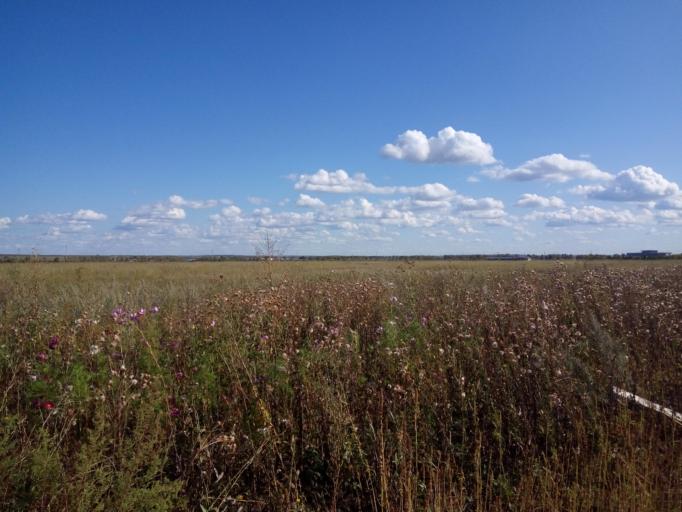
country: CN
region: Heilongjiang Sheng
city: Erjing
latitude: 48.6326
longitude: 126.1206
